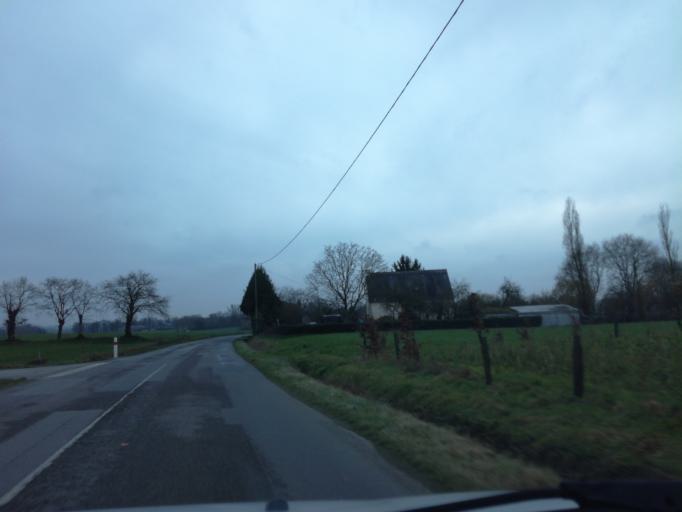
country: FR
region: Brittany
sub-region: Departement d'Ille-et-Vilaine
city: Domalain
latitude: 47.9766
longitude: -1.2710
